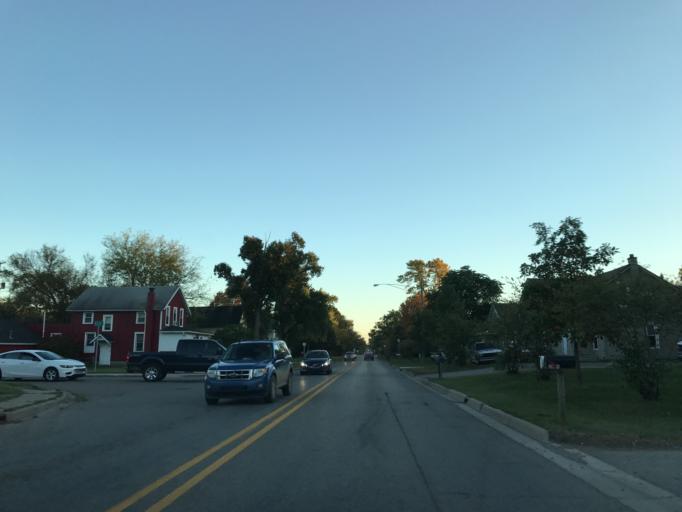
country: US
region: Michigan
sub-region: Oakland County
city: South Lyon
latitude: 42.5107
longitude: -83.6157
